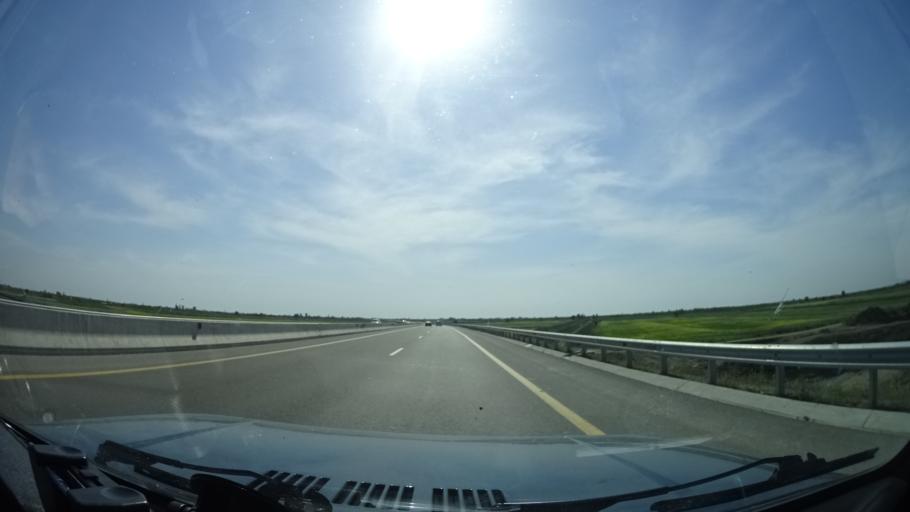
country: AZ
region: Salyan
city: Qaracala
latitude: 39.7390
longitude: 49.0851
